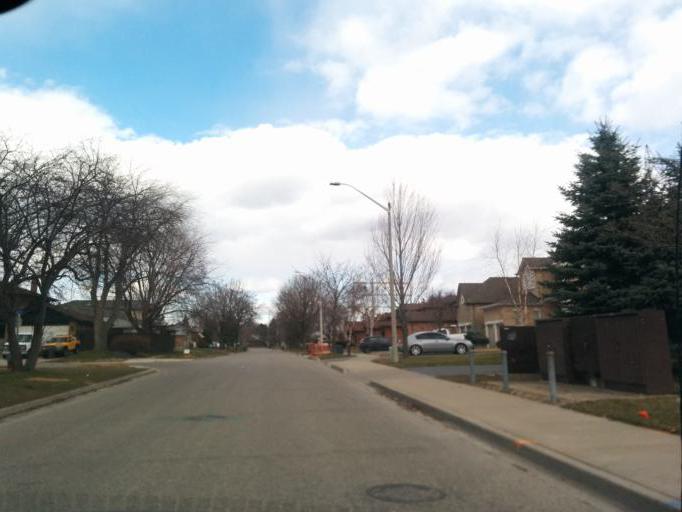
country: CA
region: Ontario
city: Etobicoke
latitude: 43.6023
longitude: -79.5726
